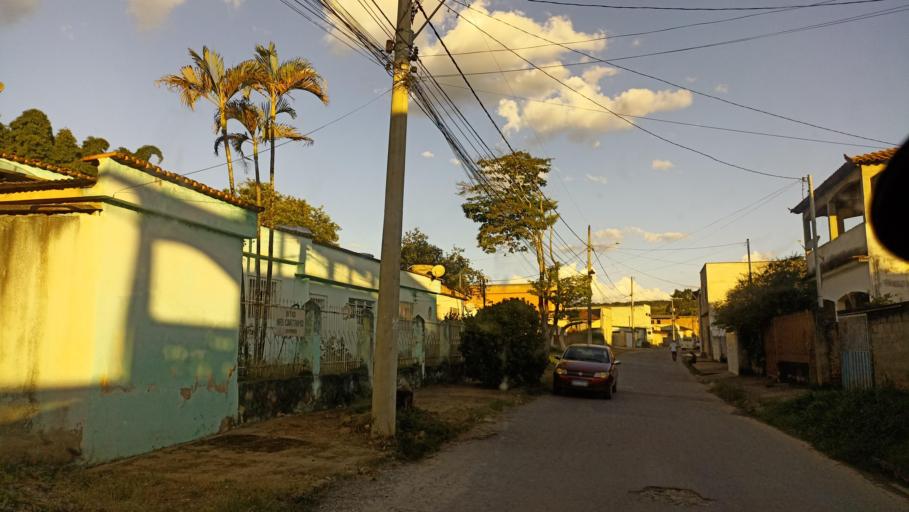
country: BR
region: Minas Gerais
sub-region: Sao Joao Del Rei
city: Sao Joao del Rei
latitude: -21.1855
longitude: -44.3312
